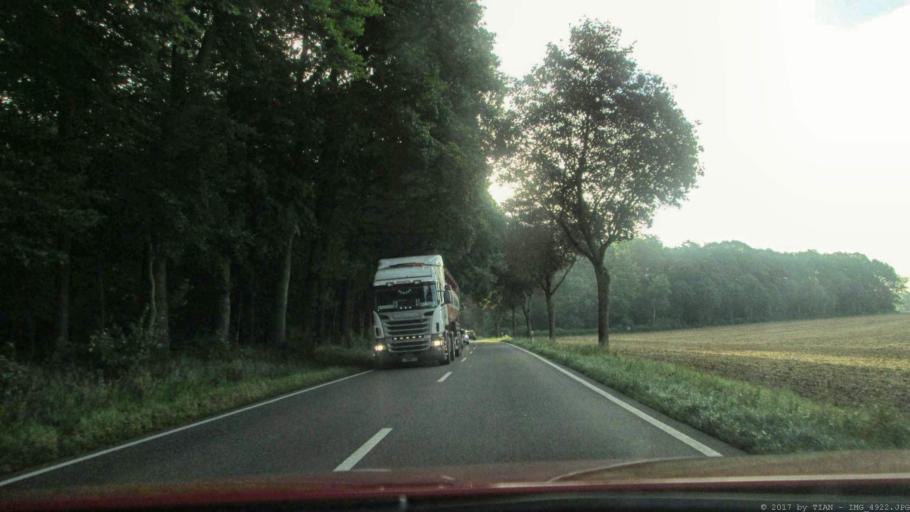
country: DE
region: Lower Saxony
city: Jelmstorf
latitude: 53.0793
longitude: 10.5421
